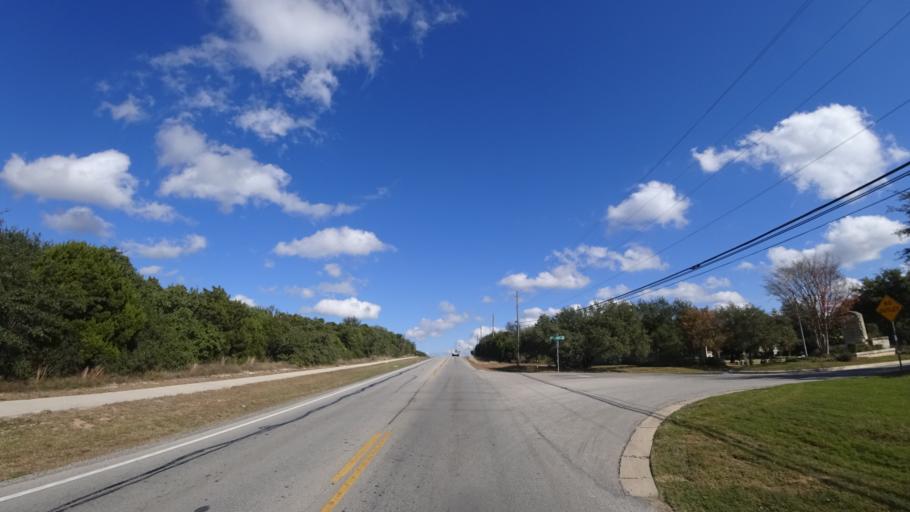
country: US
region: Texas
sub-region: Travis County
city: Barton Creek
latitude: 30.2239
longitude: -97.8915
